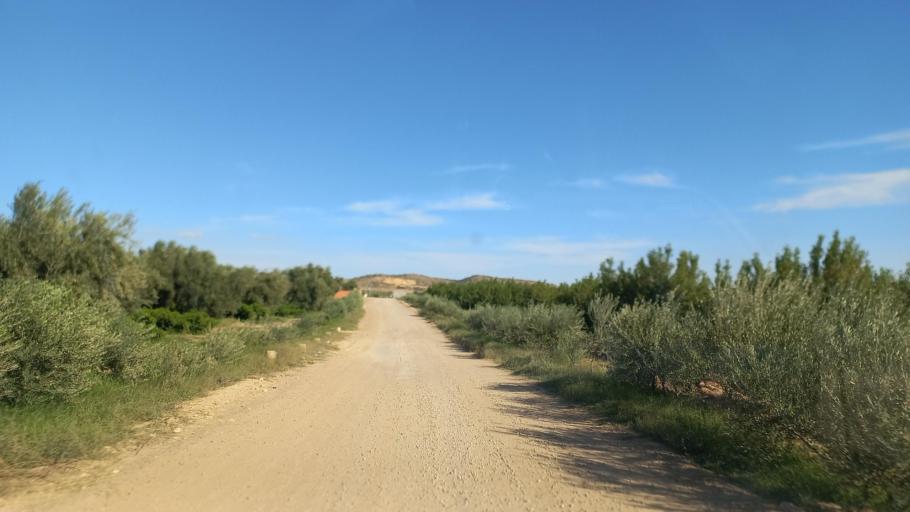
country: TN
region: Al Qasrayn
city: Sbiba
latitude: 35.2968
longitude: 9.0984
